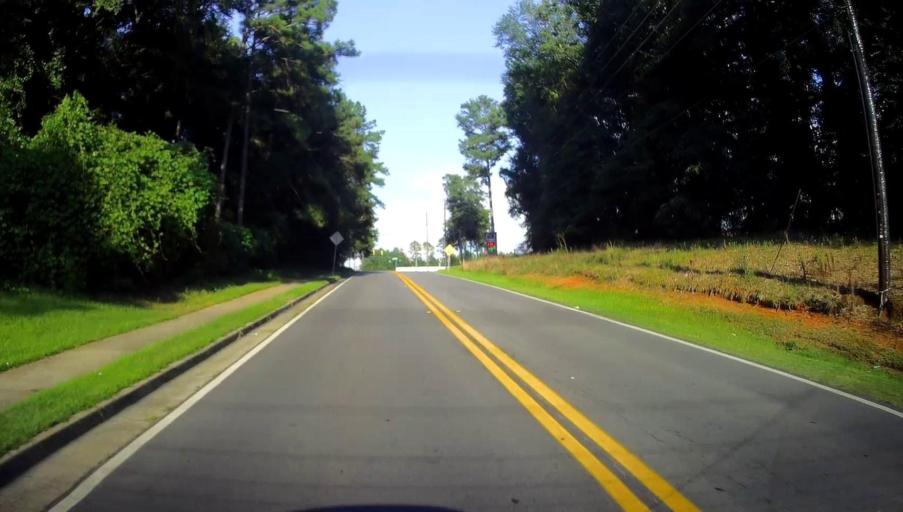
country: US
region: Georgia
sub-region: Houston County
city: Perry
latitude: 32.4684
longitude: -83.7309
